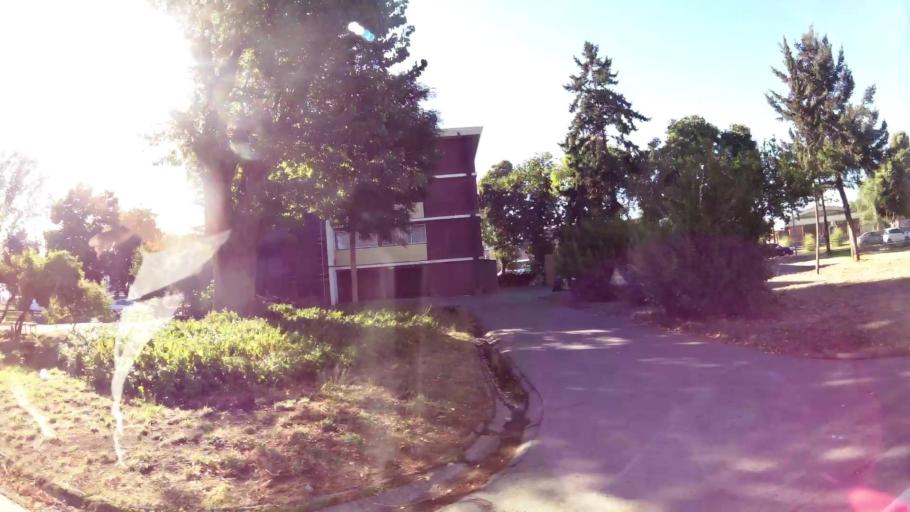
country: CL
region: Biobio
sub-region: Provincia de Concepcion
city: Concepcion
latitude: -36.8388
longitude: -73.1063
